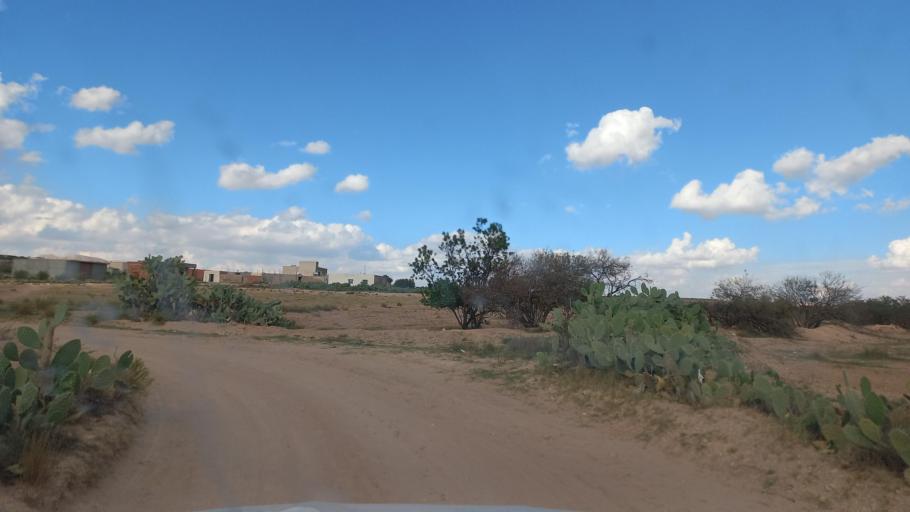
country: TN
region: Al Qasrayn
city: Sbiba
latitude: 35.3838
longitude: 9.0463
